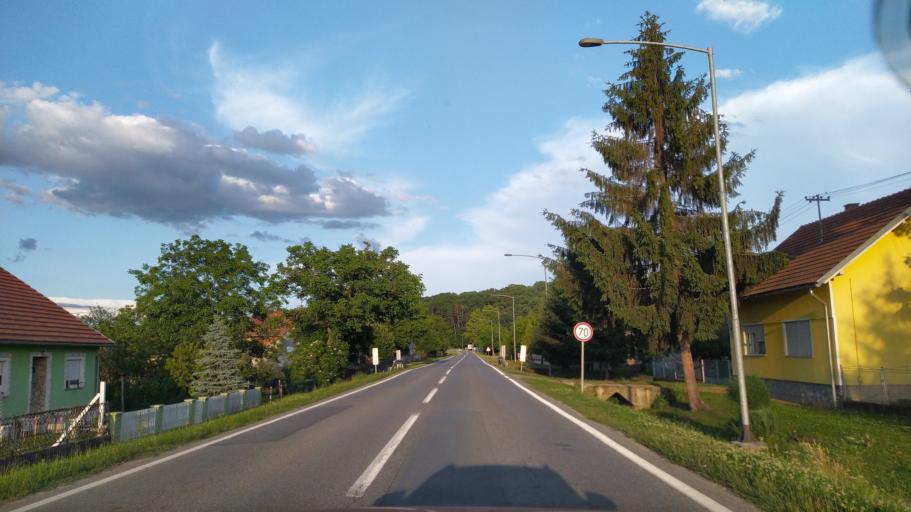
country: HR
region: Osjecko-Baranjska
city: Martin
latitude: 45.4918
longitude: 18.0240
